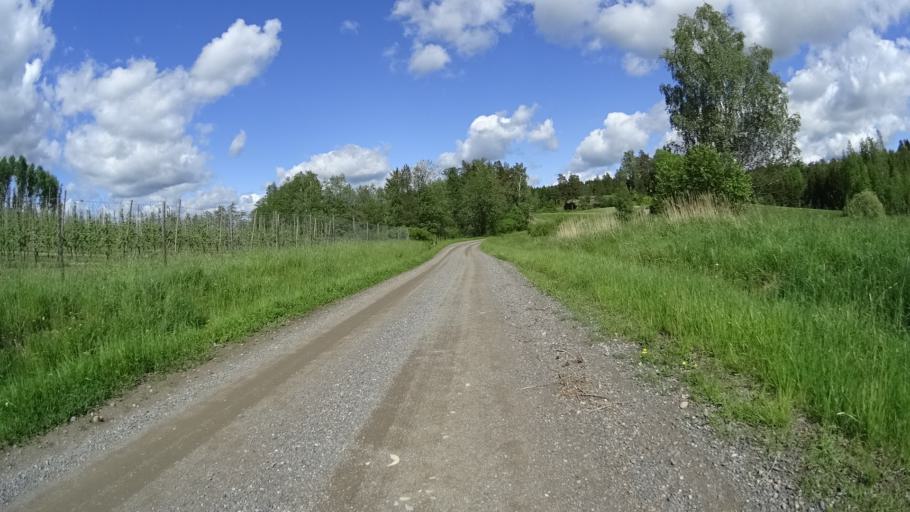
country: FI
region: Uusimaa
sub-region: Raaseporin
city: Karis
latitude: 60.1275
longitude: 23.6137
